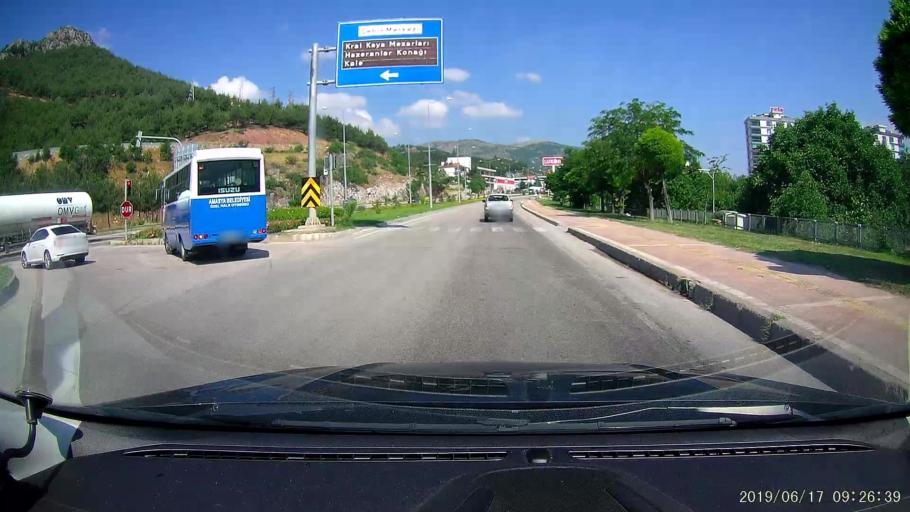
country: TR
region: Amasya
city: Amasya
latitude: 40.6705
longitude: 35.8334
